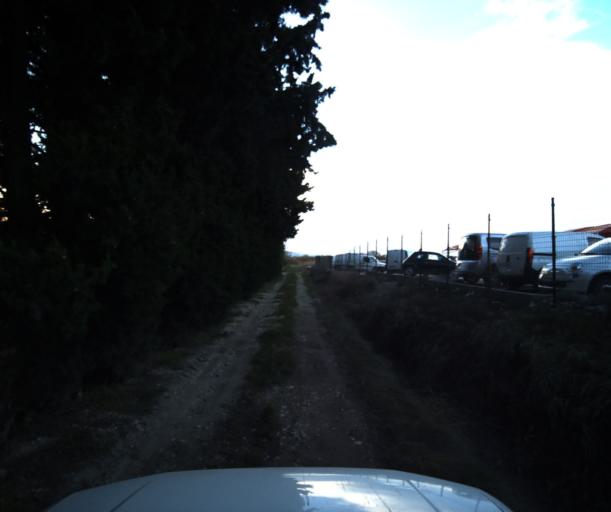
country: FR
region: Provence-Alpes-Cote d'Azur
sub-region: Departement du Vaucluse
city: Pertuis
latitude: 43.6778
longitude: 5.4962
